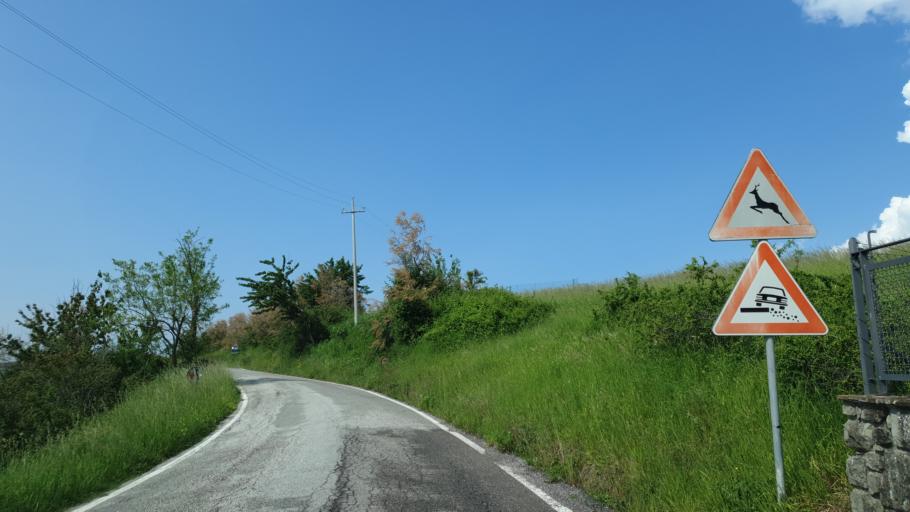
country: IT
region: Emilia-Romagna
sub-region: Provincia di Rimini
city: Sant'Agata Feltria
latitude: 43.9037
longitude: 12.2255
